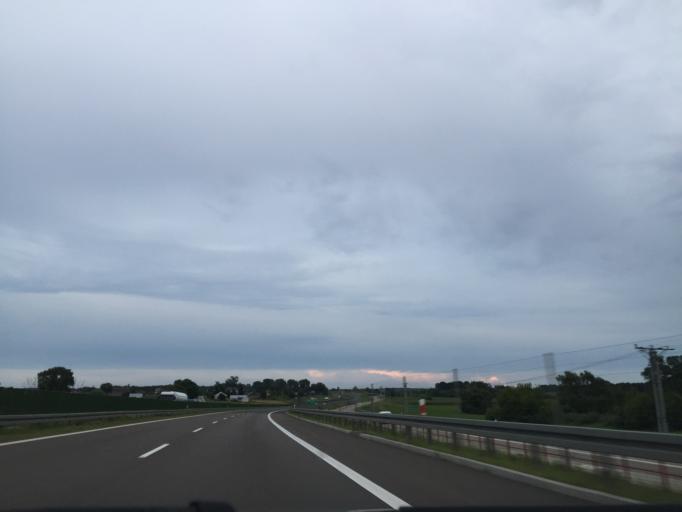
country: PL
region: Podlasie
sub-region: Powiat bialostocki
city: Choroszcz
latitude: 53.1639
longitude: 22.9638
